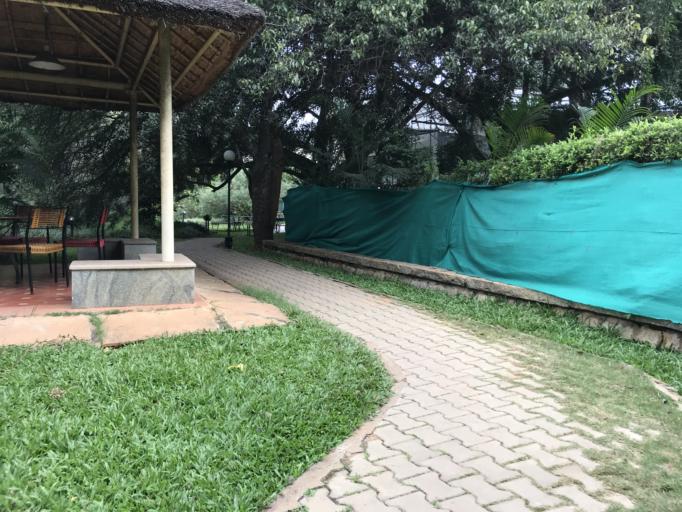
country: IN
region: Karnataka
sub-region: Bangalore Urban
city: Yelahanka
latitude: 13.0711
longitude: 77.5792
